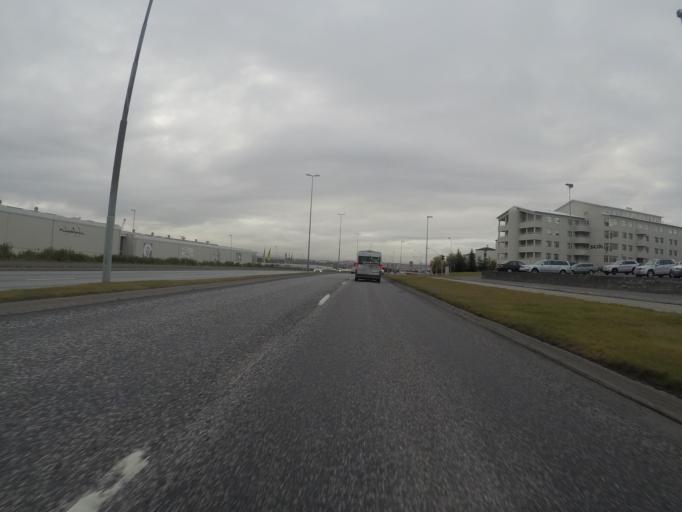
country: IS
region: Capital Region
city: Reykjavik
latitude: 64.1489
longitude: -21.8666
